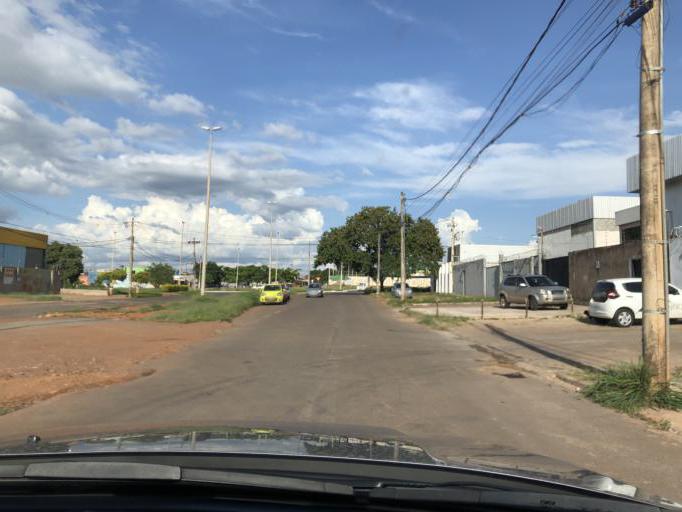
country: BR
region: Federal District
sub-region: Brasilia
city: Brasilia
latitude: -15.7909
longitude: -48.1439
